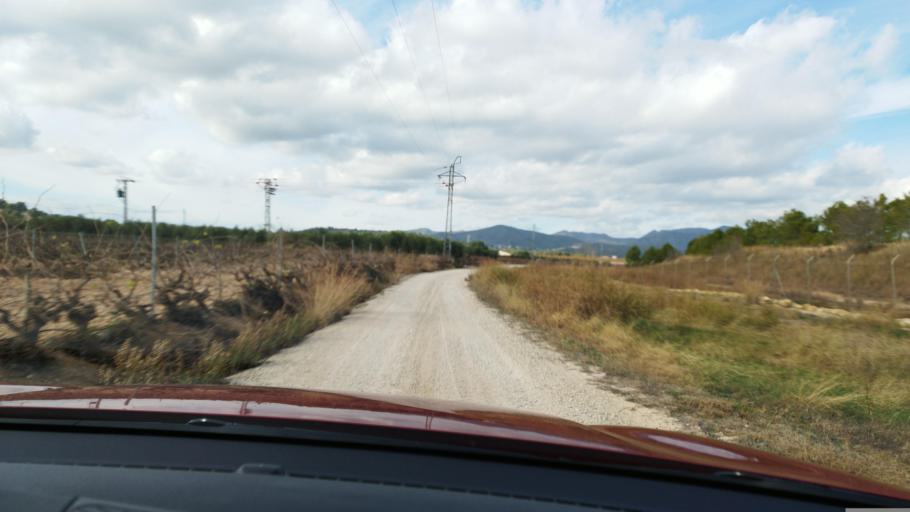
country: ES
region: Catalonia
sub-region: Provincia de Tarragona
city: Albinyana
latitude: 41.2609
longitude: 1.5015
